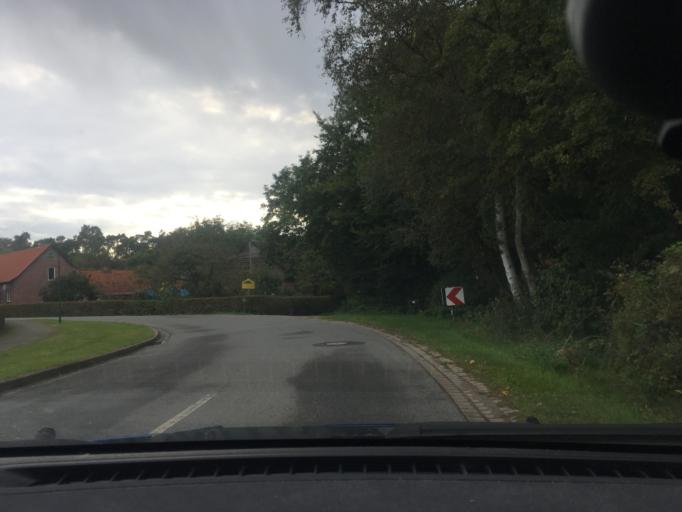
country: DE
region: Lower Saxony
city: Neu Darchau
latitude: 53.3202
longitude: 10.9077
